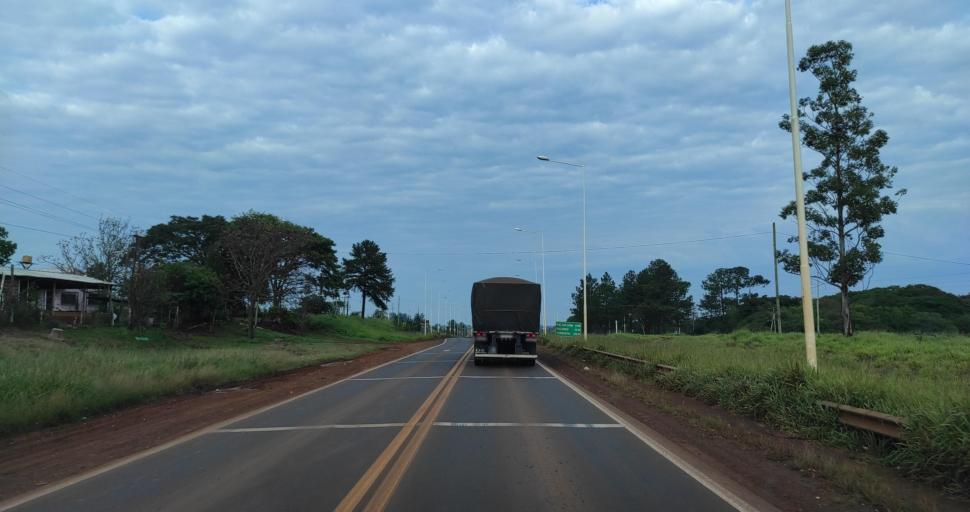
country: AR
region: Corrientes
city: Gobernador Ingeniero Valentin Virasoro
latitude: -27.9653
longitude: -56.0069
